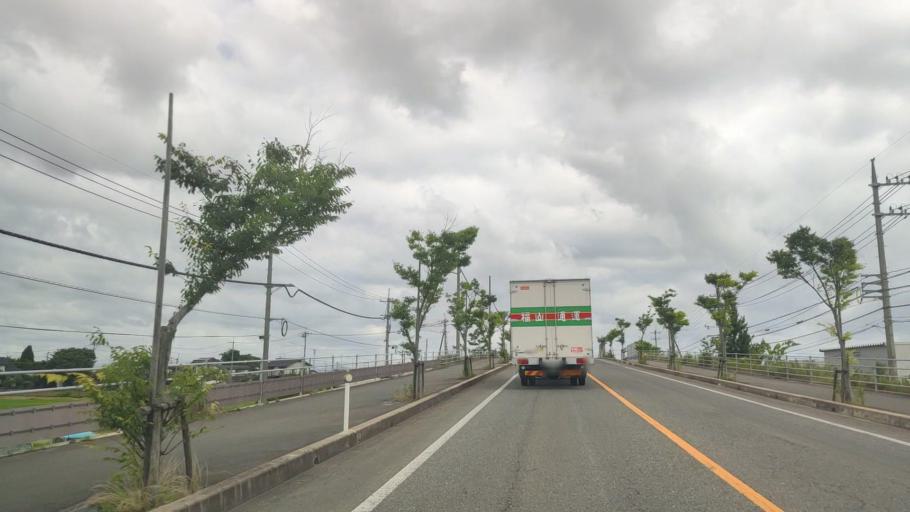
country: JP
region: Tottori
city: Yonago
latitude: 35.4329
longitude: 133.3918
